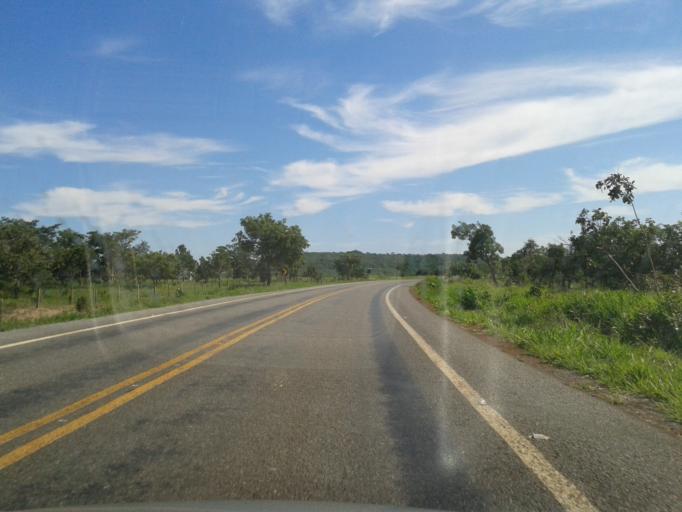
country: BR
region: Goias
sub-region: Piracanjuba
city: Piracanjuba
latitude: -17.2920
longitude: -48.7875
